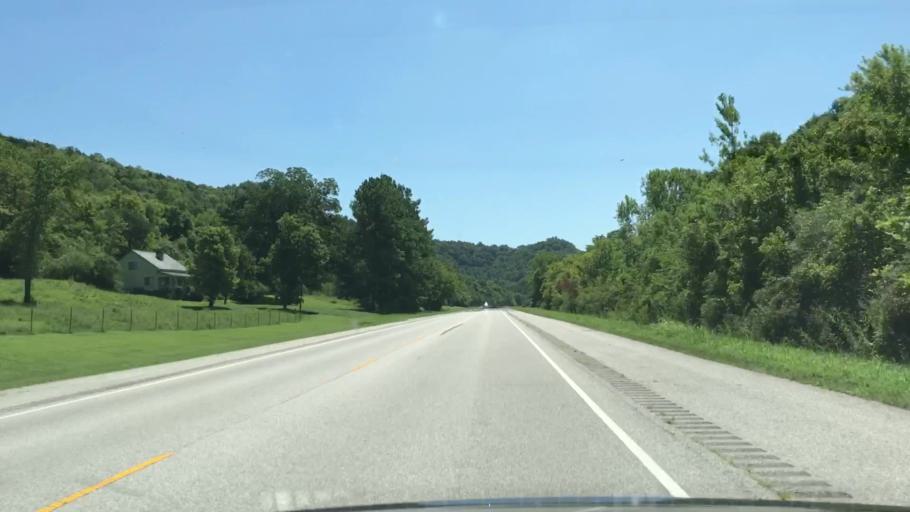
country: US
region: Tennessee
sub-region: Jackson County
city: Gainesboro
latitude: 36.4069
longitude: -85.6370
